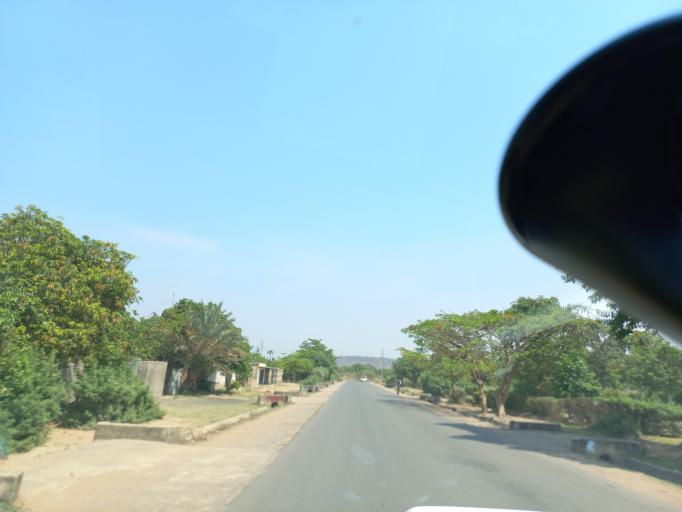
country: ZM
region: Lusaka
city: Kafue
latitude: -15.7428
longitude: 28.1753
